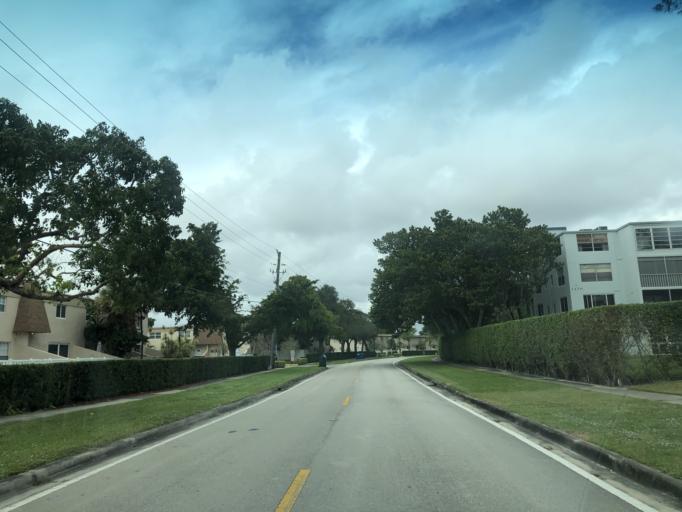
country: US
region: Florida
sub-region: Broward County
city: Margate
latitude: 26.2464
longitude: -80.2329
